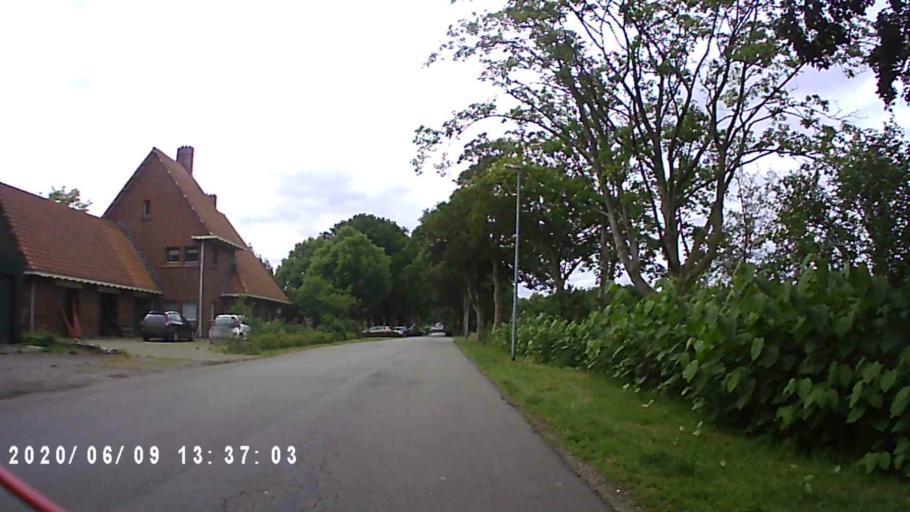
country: NL
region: Groningen
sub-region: Gemeente Haren
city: Haren
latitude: 53.2079
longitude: 6.6532
